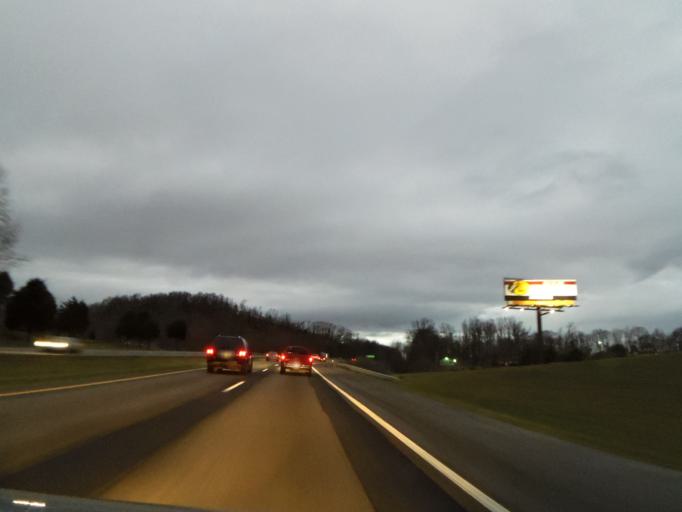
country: US
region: Tennessee
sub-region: Washington County
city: Oak Grove
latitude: 36.3870
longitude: -82.4379
